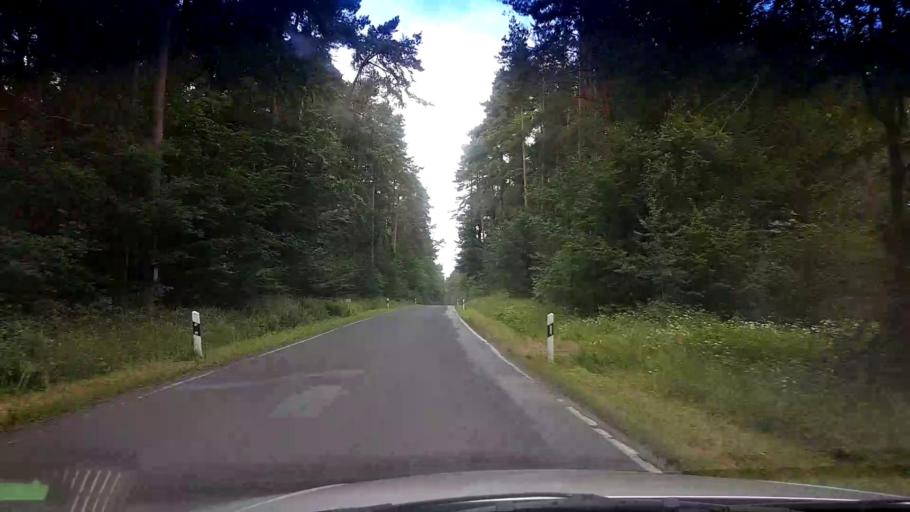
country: DE
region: Bavaria
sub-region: Upper Franconia
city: Oberhaid
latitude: 49.9450
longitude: 10.8162
